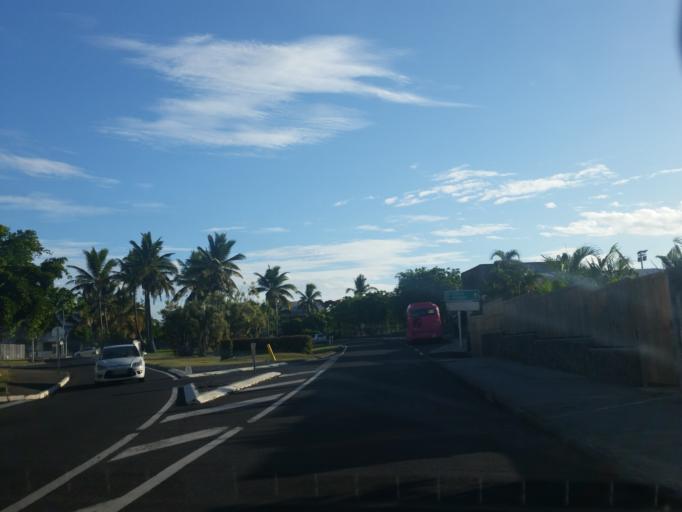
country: RE
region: Reunion
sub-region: Reunion
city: Les Avirons
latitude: -21.2713
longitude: 55.3344
